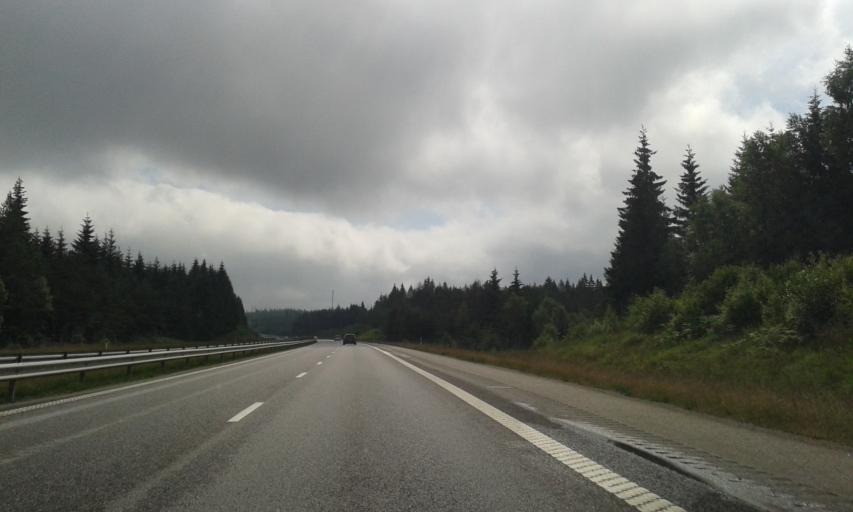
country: SE
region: Vaestra Goetaland
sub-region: Harryda Kommun
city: Hindas
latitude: 57.6686
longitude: 12.3838
